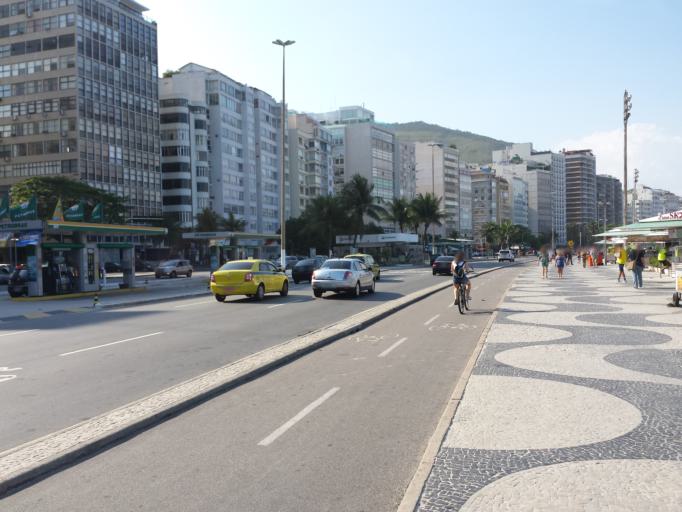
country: BR
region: Rio de Janeiro
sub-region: Rio De Janeiro
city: Rio de Janeiro
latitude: -22.9843
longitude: -43.1893
